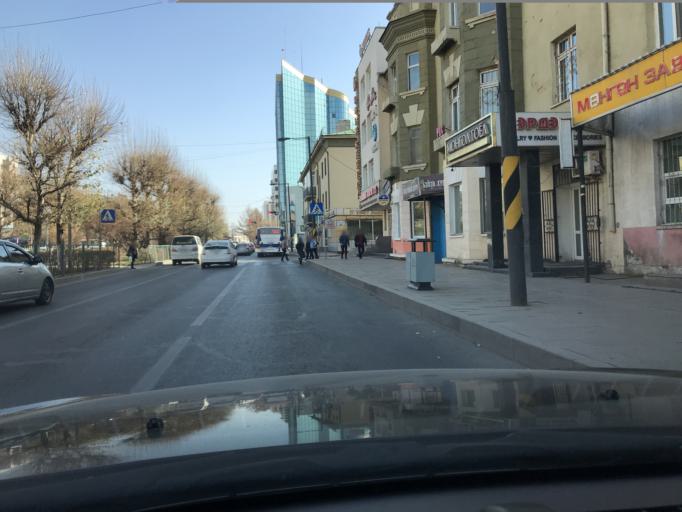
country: MN
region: Ulaanbaatar
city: Ulaanbaatar
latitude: 47.9220
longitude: 106.9092
